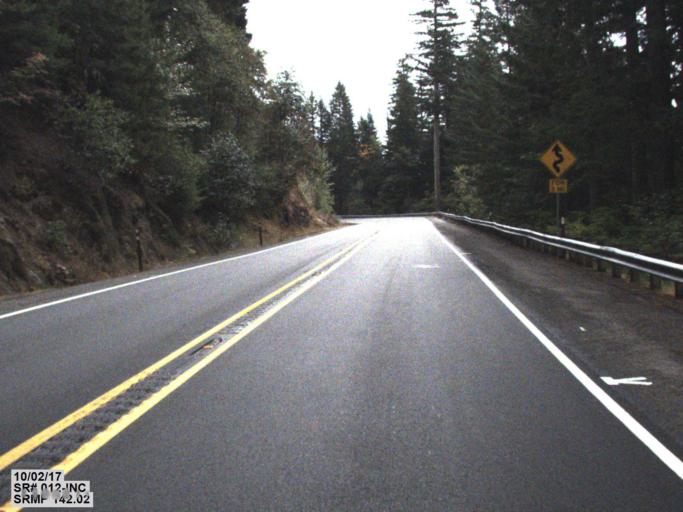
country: US
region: Washington
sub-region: Pierce County
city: Buckley
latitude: 46.6787
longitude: -121.5315
